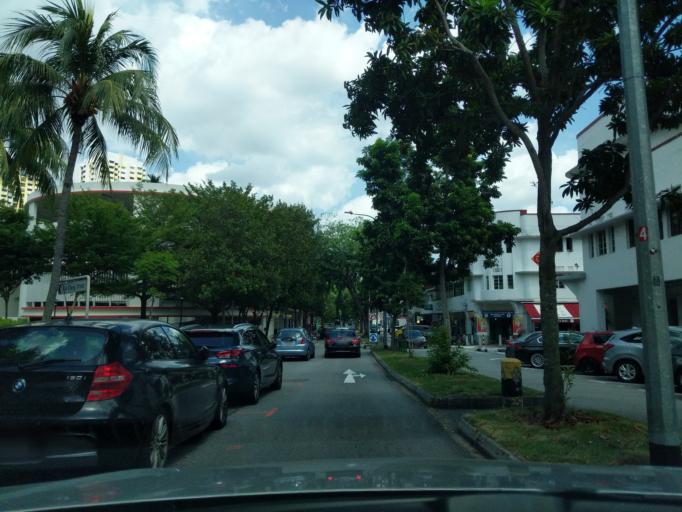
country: SG
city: Singapore
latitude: 1.2840
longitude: 103.8318
